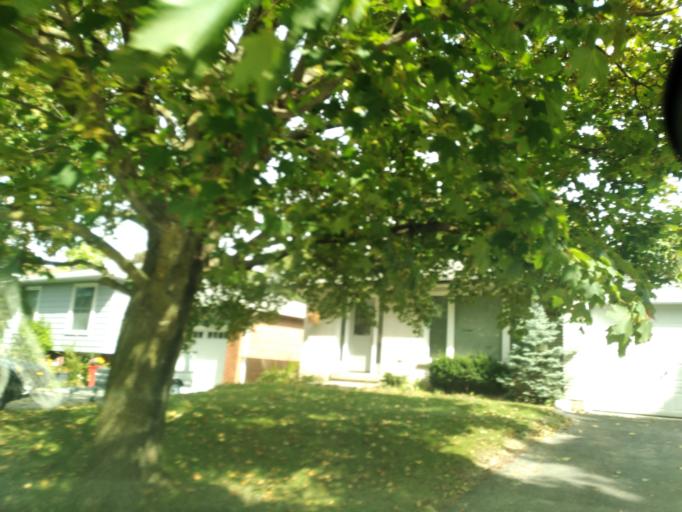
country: CA
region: Ontario
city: Newmarket
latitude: 44.0994
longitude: -79.4847
